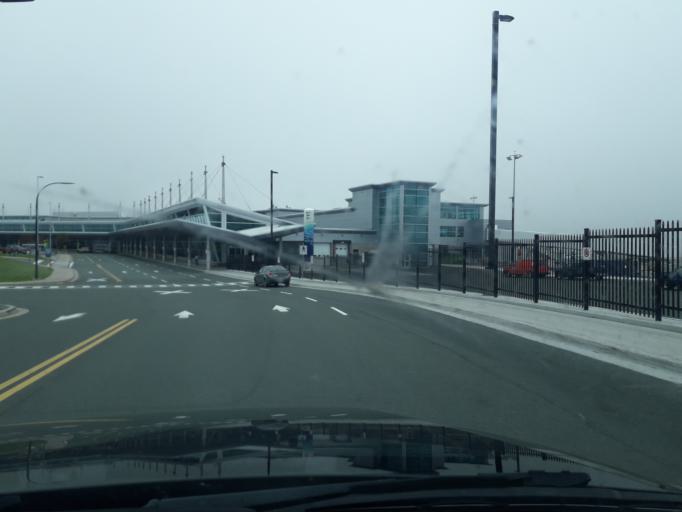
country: CA
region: Newfoundland and Labrador
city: Torbay
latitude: 47.6111
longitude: -52.7418
